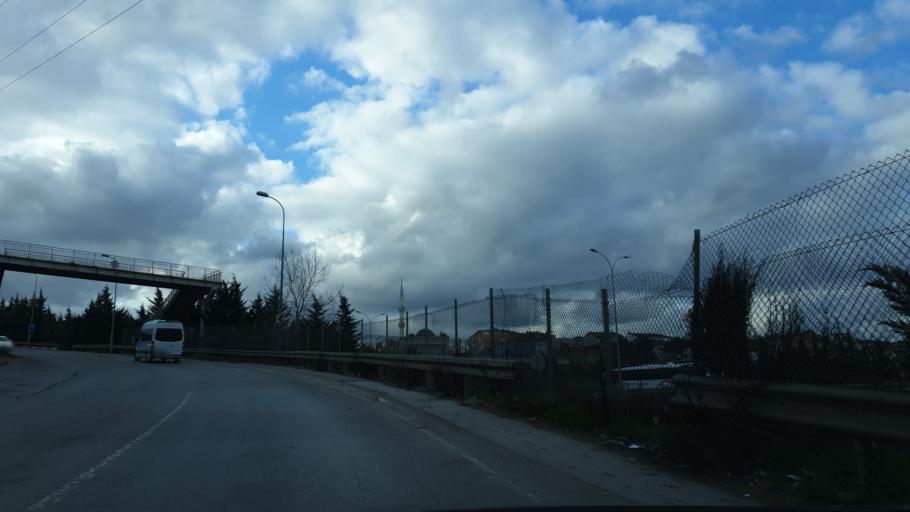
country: TR
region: Istanbul
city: Sultanbeyli
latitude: 40.9508
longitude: 29.3034
